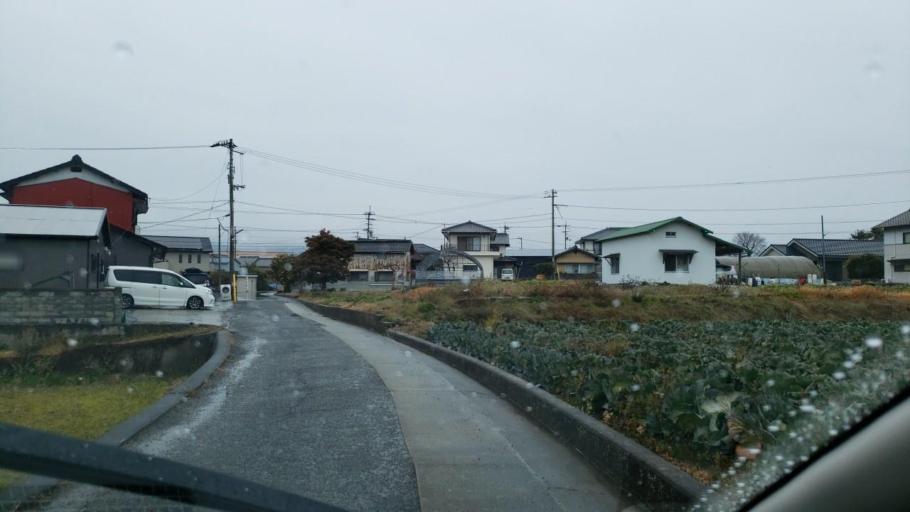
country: JP
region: Tokushima
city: Kamojimacho-jogejima
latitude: 34.0786
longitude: 134.2567
